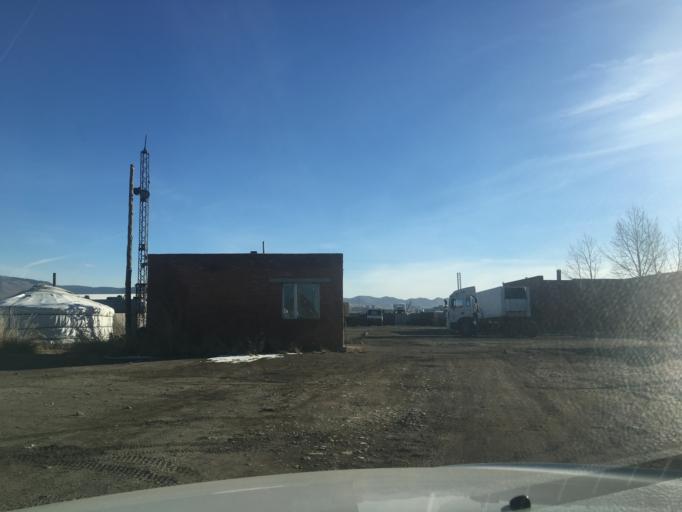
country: MN
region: Ulaanbaatar
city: Ulaanbaatar
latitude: 47.9008
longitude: 106.7754
